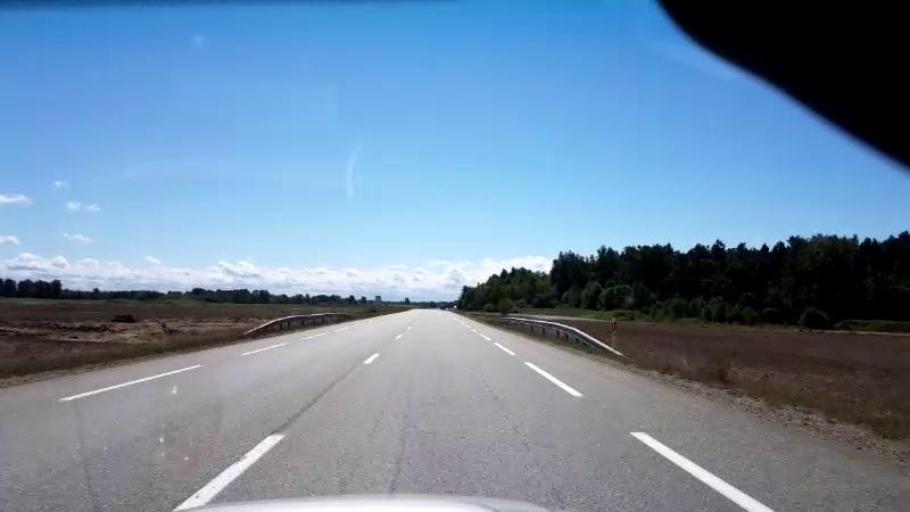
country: LV
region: Saulkrastu
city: Saulkrasti
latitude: 57.4127
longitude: 24.4310
